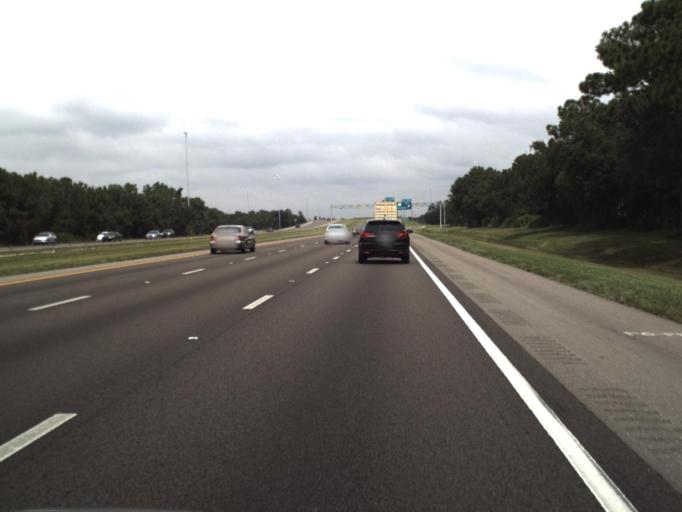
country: US
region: Florida
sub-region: Sarasota County
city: Desoto Lakes
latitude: 27.4332
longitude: -82.4593
